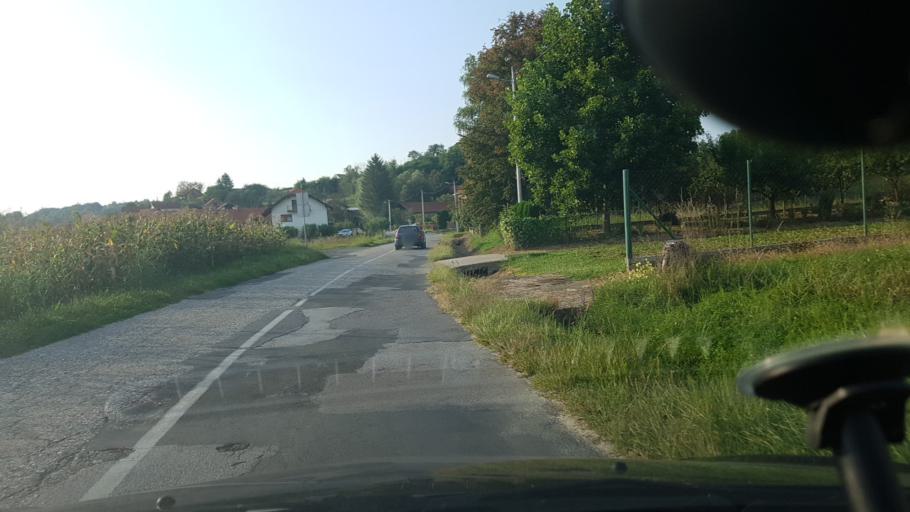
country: HR
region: Krapinsko-Zagorska
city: Zabok
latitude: 46.0319
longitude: 15.8589
